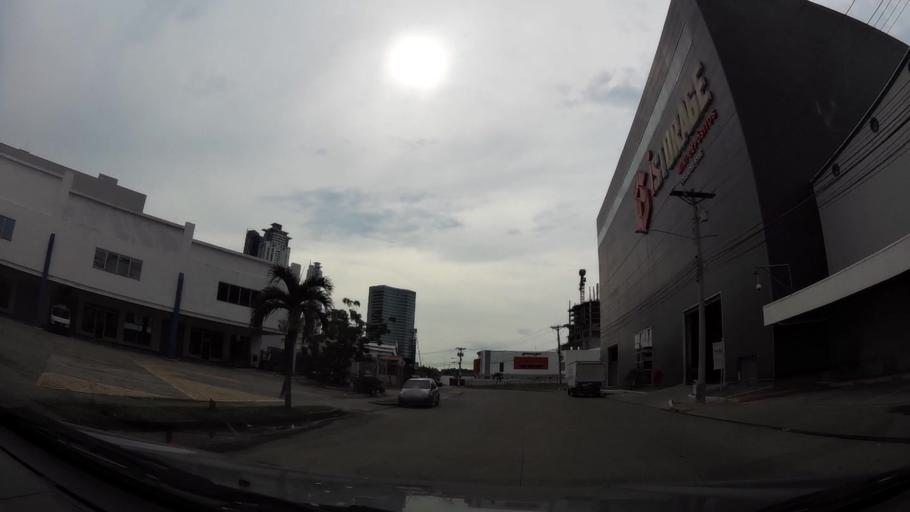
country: PA
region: Panama
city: San Miguelito
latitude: 9.0116
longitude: -79.4823
